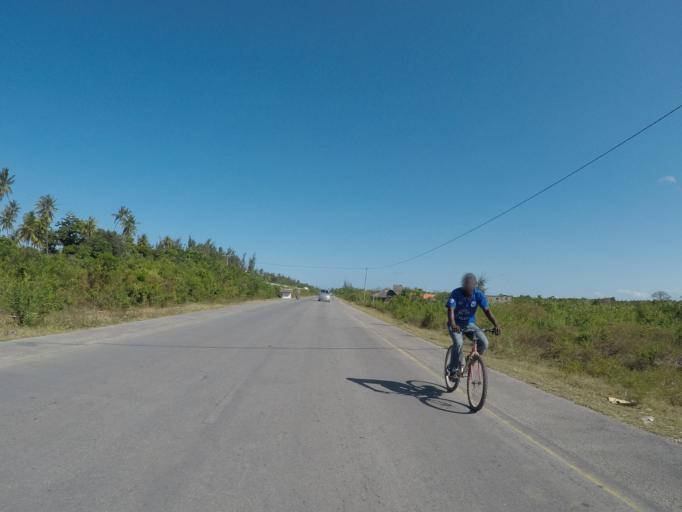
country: TZ
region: Zanzibar Central/South
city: Nganane
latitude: -6.2753
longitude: 39.5335
